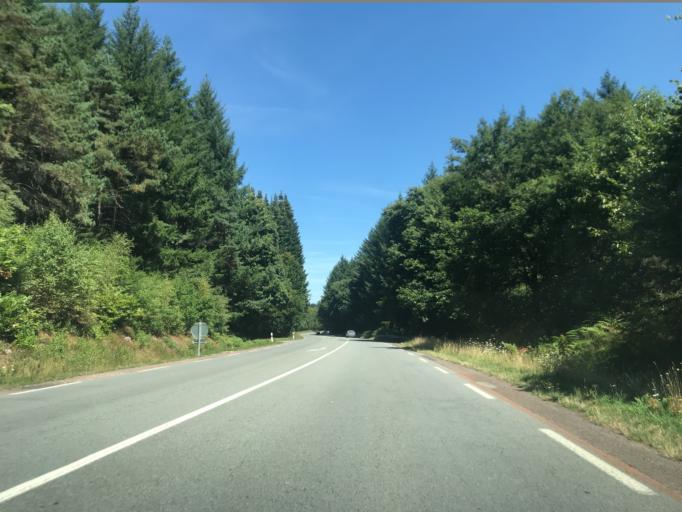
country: FR
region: Limousin
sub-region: Departement de la Correze
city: Egletons
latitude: 45.3641
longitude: 1.9913
